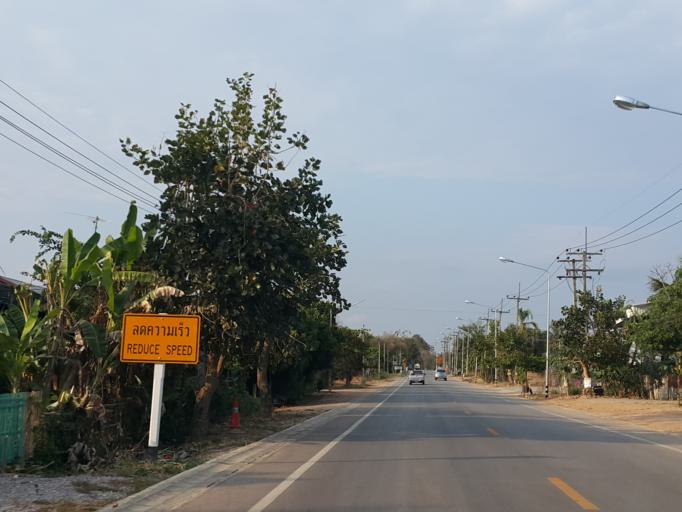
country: TH
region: Lampang
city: Chae Hom
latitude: 18.5295
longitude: 99.4778
